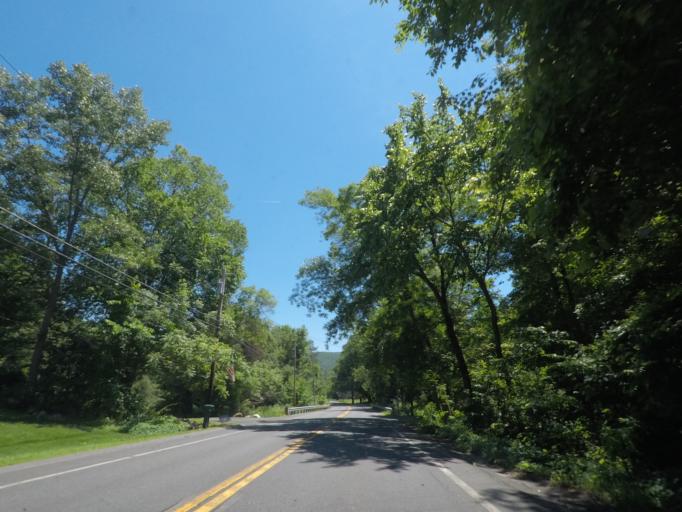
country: US
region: Massachusetts
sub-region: Berkshire County
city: Becket
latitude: 42.2694
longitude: -72.9671
